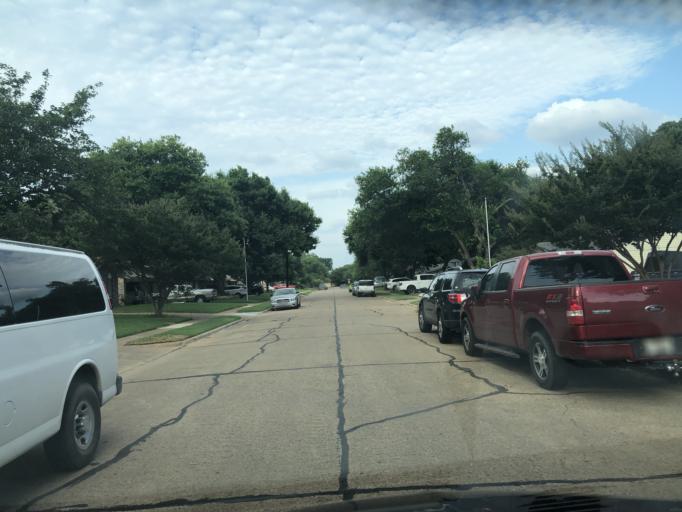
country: US
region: Texas
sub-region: Dallas County
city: Irving
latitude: 32.7883
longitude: -96.9719
